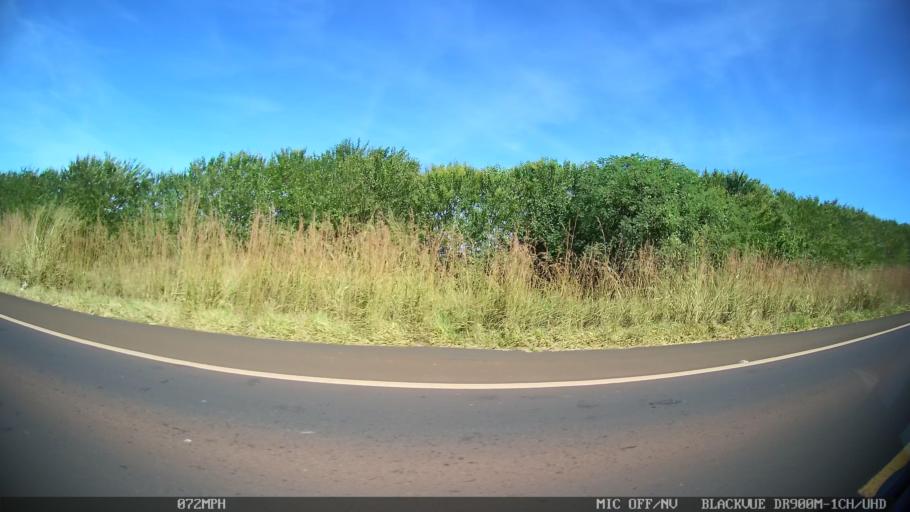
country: BR
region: Sao Paulo
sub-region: Franca
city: Franca
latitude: -20.5588
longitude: -47.5440
